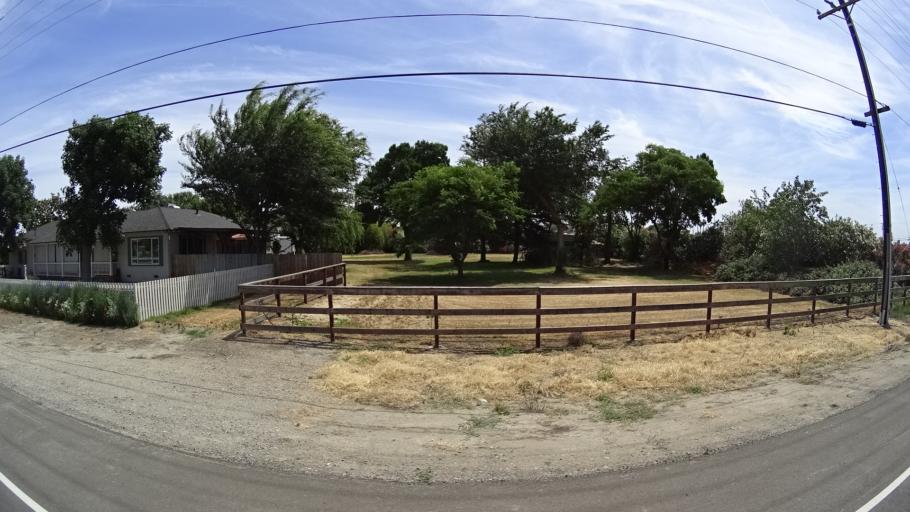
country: US
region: California
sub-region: Kings County
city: Armona
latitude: 36.3293
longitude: -119.6910
